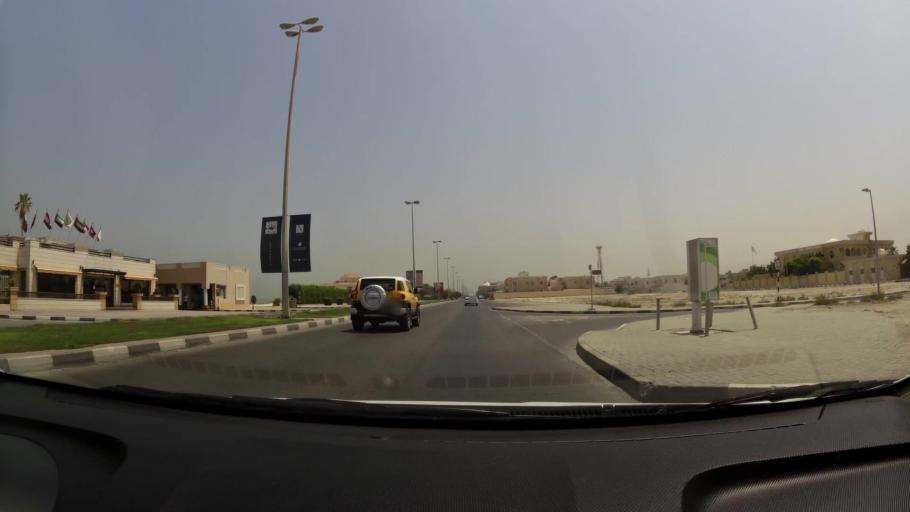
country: AE
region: Ash Shariqah
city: Sharjah
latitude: 25.3412
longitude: 55.3646
